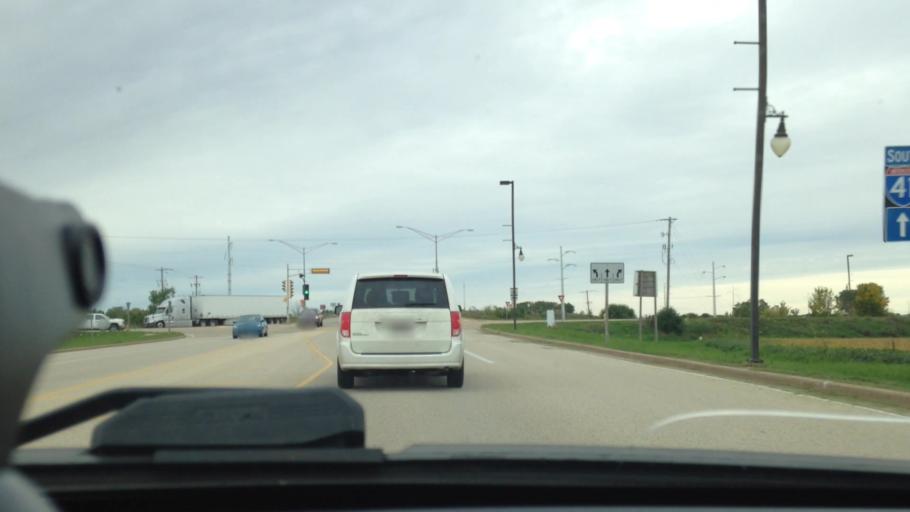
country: US
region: Wisconsin
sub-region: Fond du Lac County
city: North Fond du Lac
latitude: 43.8065
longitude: -88.4943
